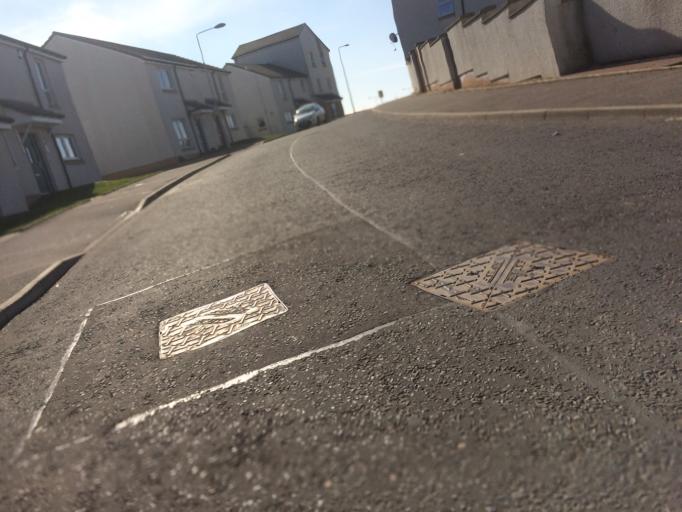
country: GB
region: Scotland
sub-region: Fife
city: Kirkcaldy
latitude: 56.1375
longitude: -3.1937
